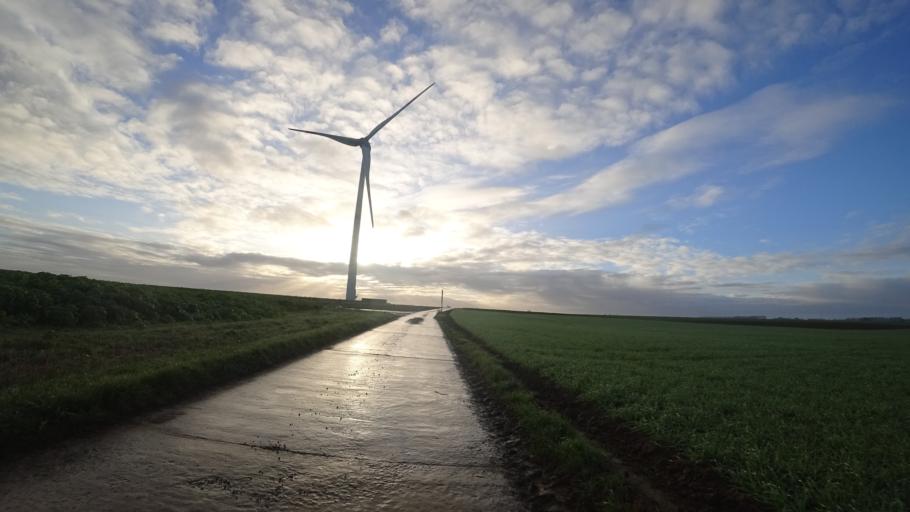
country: BE
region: Wallonia
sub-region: Province de Namur
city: Gembloux
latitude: 50.5925
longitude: 4.6905
